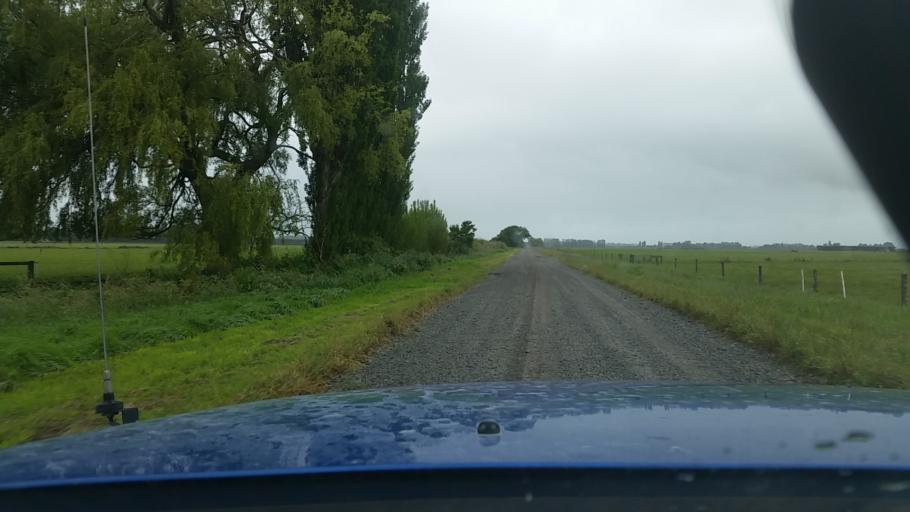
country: NZ
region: Canterbury
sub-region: Ashburton District
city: Tinwald
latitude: -43.9997
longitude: 171.6478
